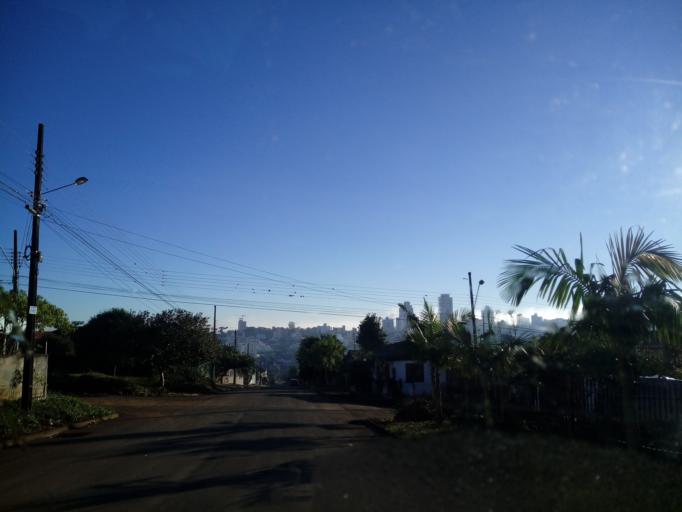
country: BR
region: Santa Catarina
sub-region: Chapeco
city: Chapeco
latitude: -27.1206
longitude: -52.6213
